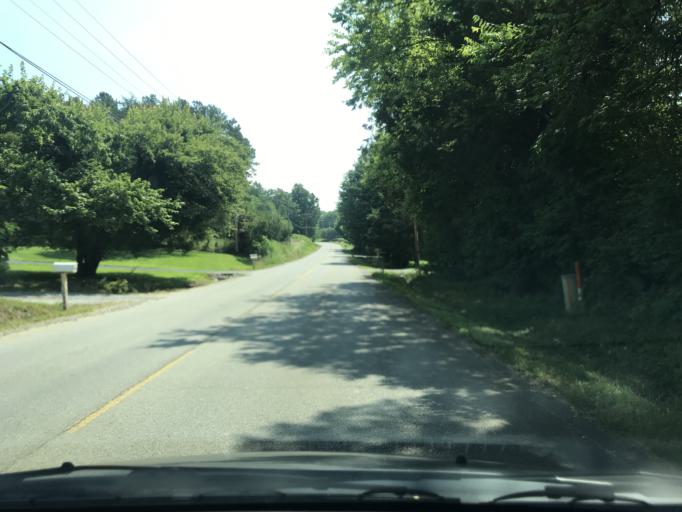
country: US
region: Tennessee
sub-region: Loudon County
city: Lenoir City
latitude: 35.8326
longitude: -84.3068
